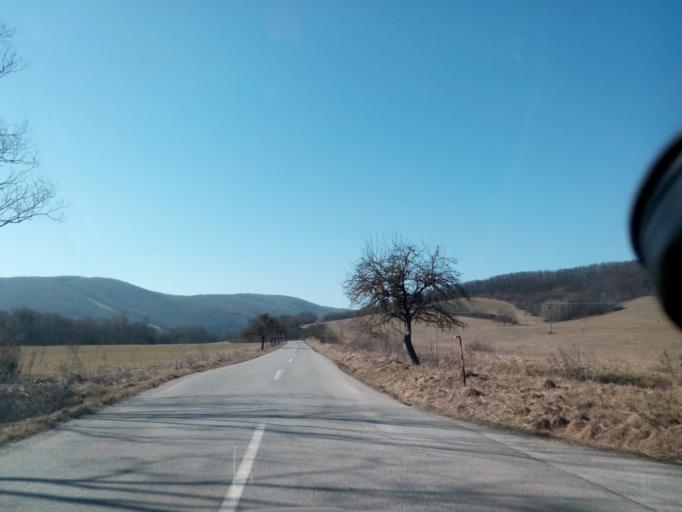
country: SK
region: Kosicky
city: Roznava
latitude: 48.5734
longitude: 20.6430
